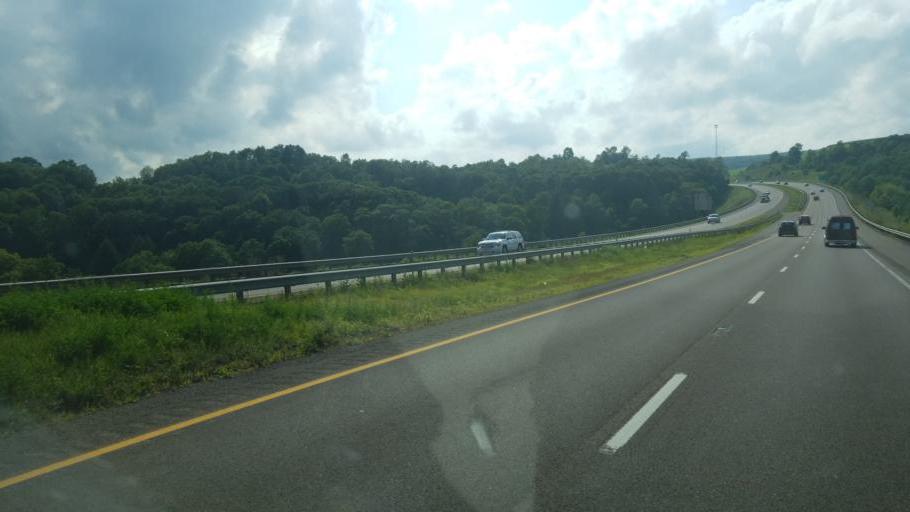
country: US
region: Pennsylvania
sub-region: Somerset County
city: Meyersdale
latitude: 39.6940
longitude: -79.1714
